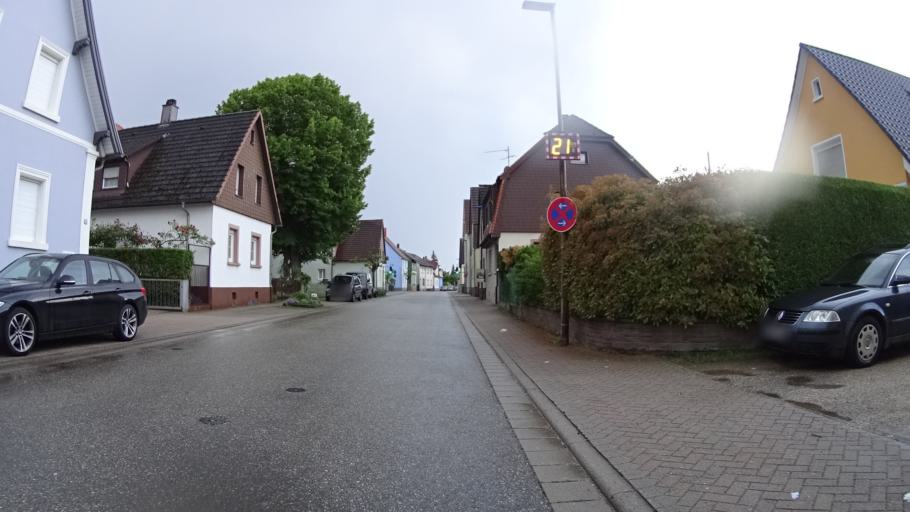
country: DE
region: Baden-Wuerttemberg
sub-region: Karlsruhe Region
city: Durmersheim
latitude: 48.9282
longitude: 8.2686
